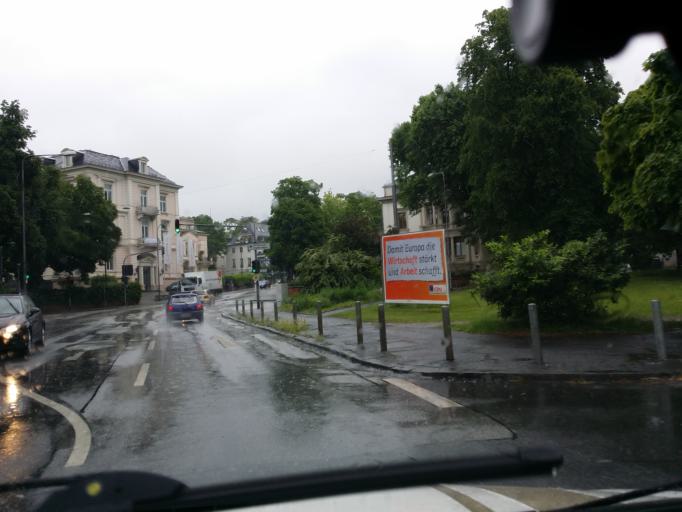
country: DE
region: Hesse
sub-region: Regierungsbezirk Darmstadt
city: Wiesbaden
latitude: 50.0795
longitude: 8.2463
